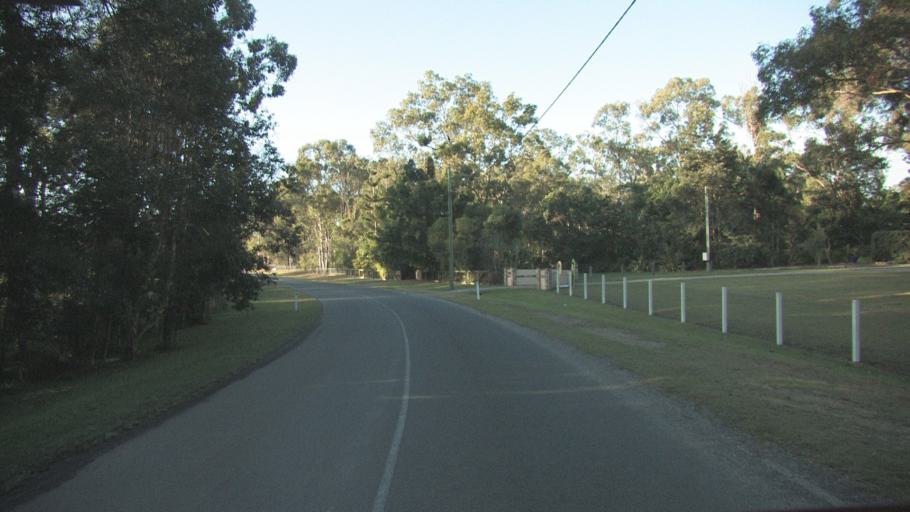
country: AU
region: Queensland
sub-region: Logan
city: Waterford West
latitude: -27.7284
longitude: 153.1405
